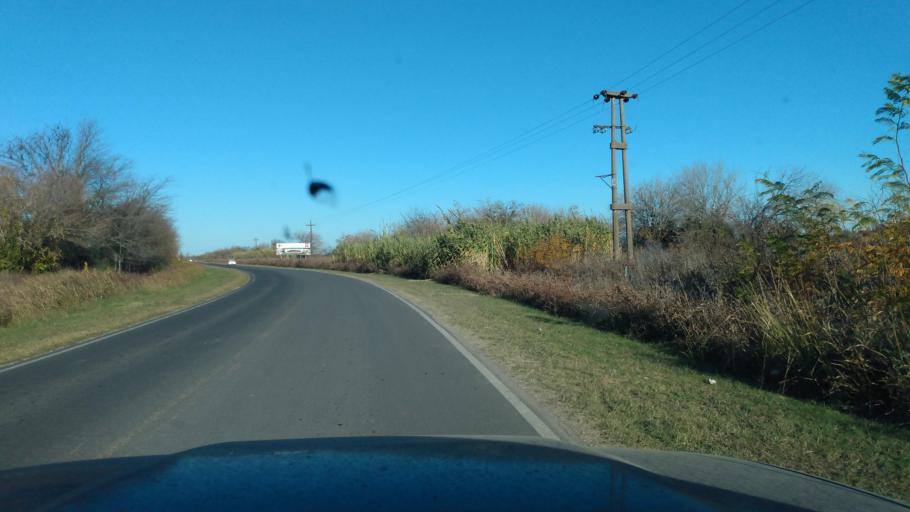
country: AR
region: Buenos Aires
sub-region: Partido de Lujan
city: Lujan
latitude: -34.4941
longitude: -59.2087
